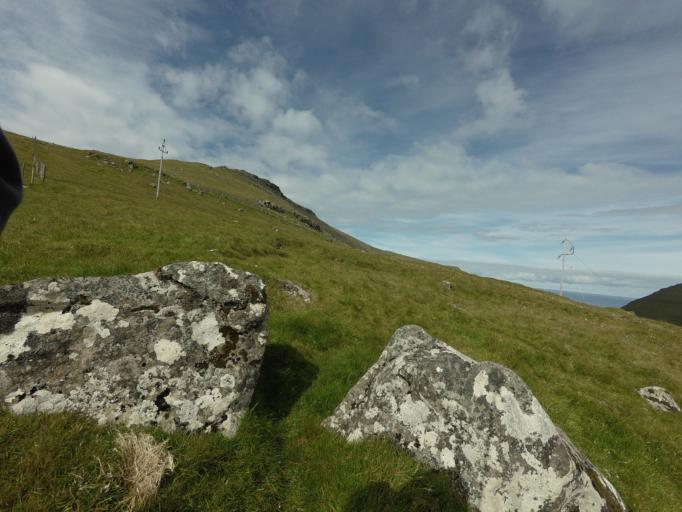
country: FO
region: Nordoyar
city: Klaksvik
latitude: 62.3229
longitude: -6.2848
